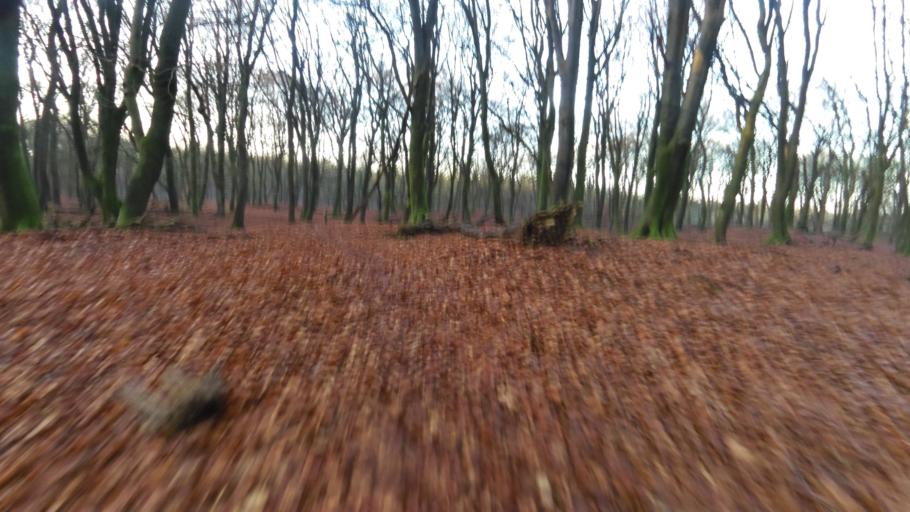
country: NL
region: Gelderland
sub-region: Gemeente Apeldoorn
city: Uddel
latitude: 52.2291
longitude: 5.8122
